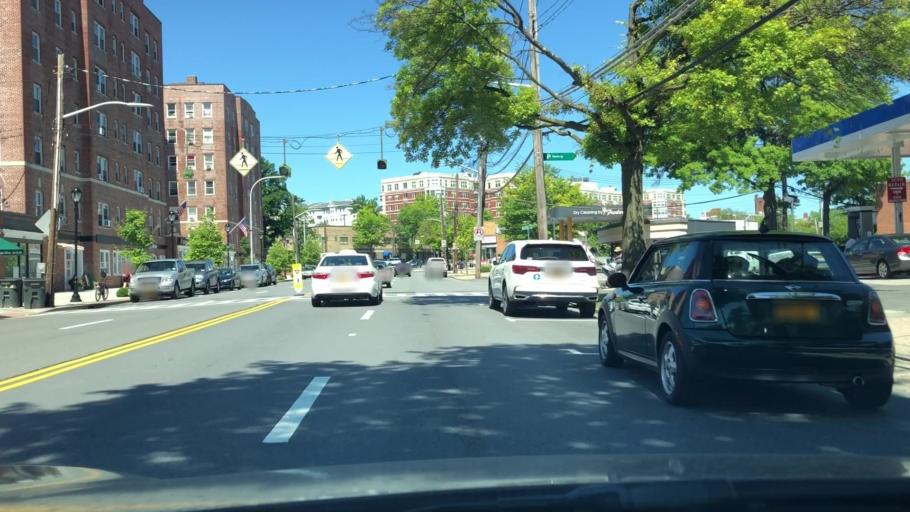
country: US
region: New York
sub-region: Westchester County
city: White Plains
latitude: 41.0233
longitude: -73.7611
